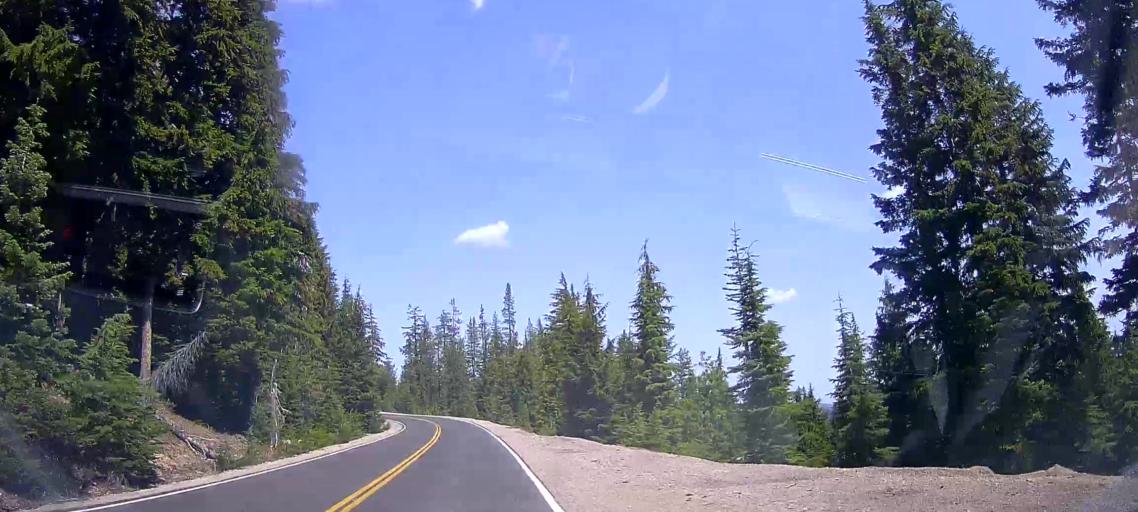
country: US
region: Oregon
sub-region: Jackson County
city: Shady Cove
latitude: 42.9797
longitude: -122.1071
